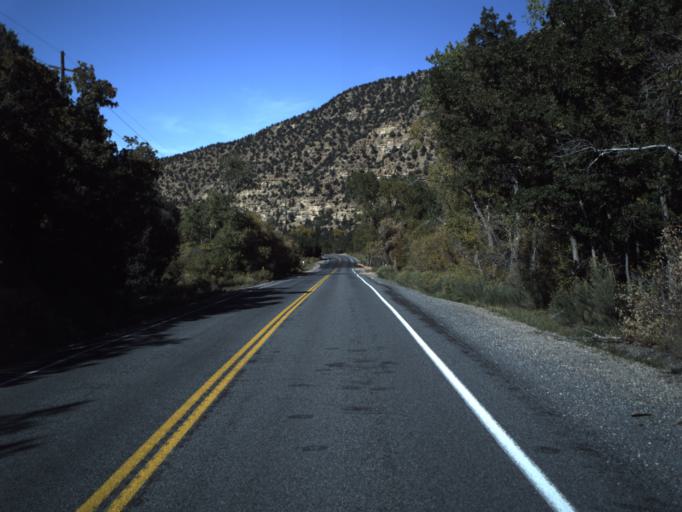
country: US
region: Utah
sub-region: Iron County
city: Parowan
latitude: 37.8057
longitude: -112.8110
